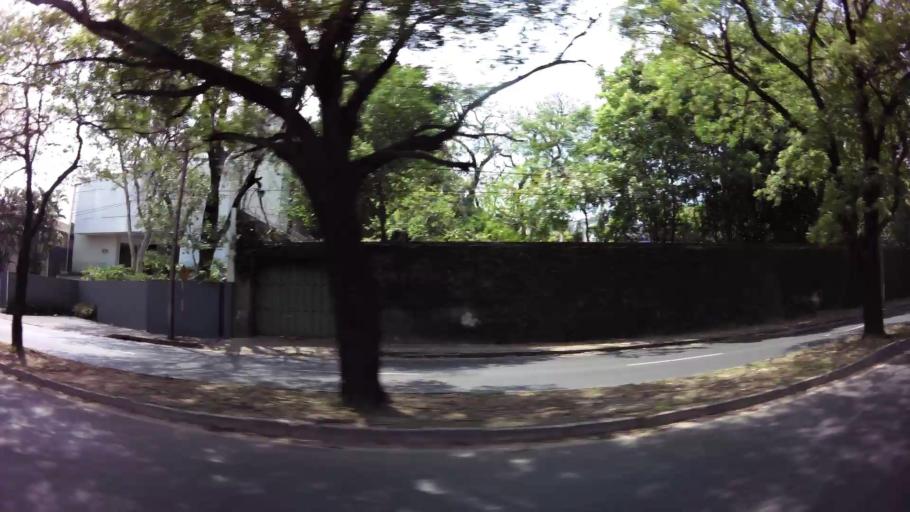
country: PY
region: Asuncion
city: Asuncion
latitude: -25.2791
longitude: -57.5865
